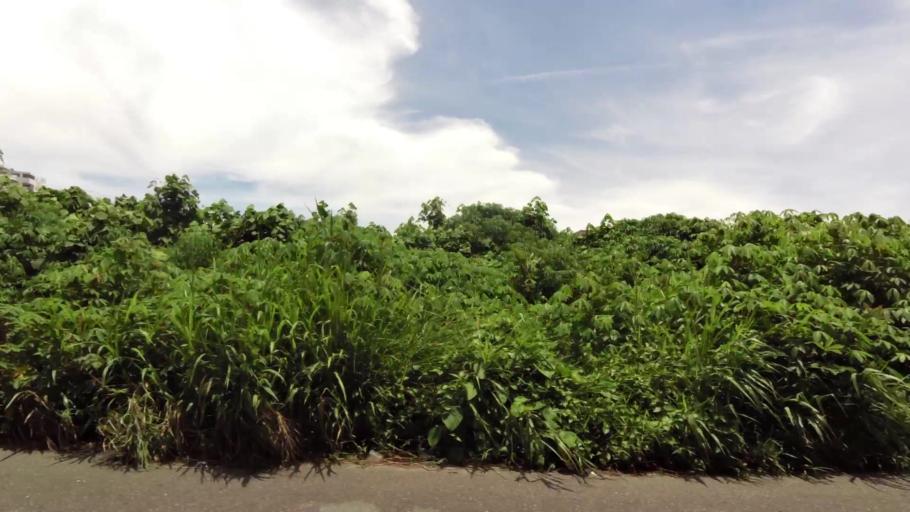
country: BN
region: Belait
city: Kuala Belait
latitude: 4.5932
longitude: 114.2471
